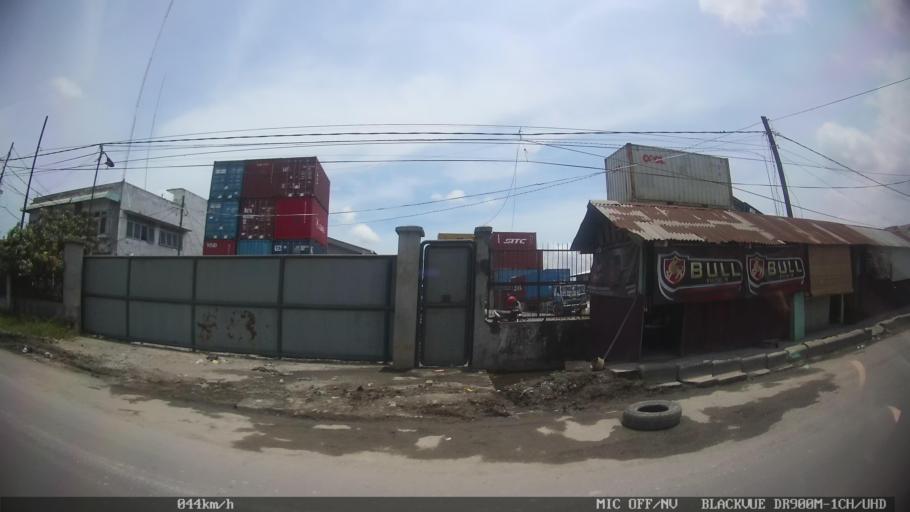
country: ID
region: North Sumatra
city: Labuhan Deli
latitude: 3.7178
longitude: 98.6802
